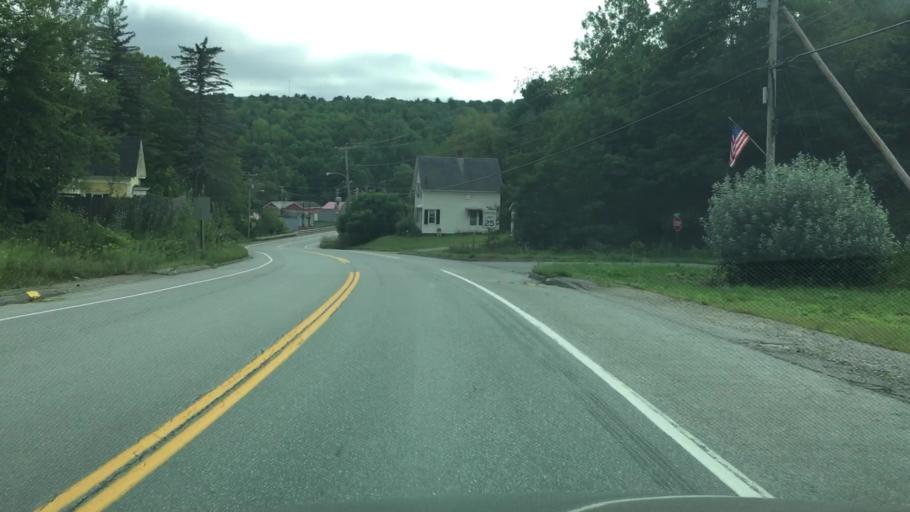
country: US
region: Maine
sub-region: Waldo County
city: Frankfort
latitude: 44.6109
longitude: -68.8721
